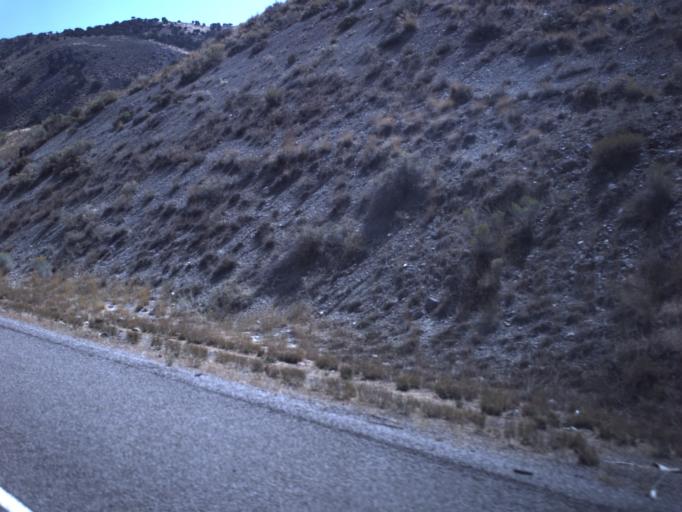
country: US
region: Utah
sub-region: Sevier County
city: Salina
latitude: 38.9304
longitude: -111.8357
